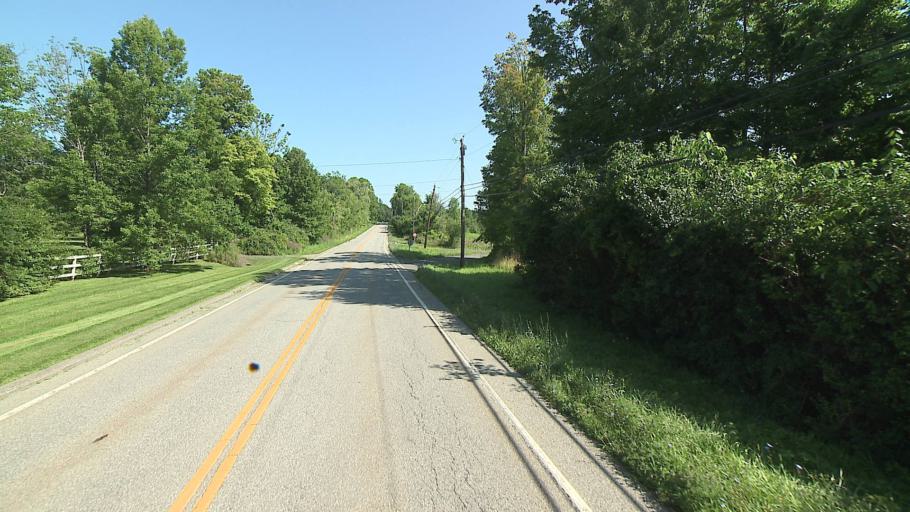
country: US
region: Connecticut
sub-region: Litchfield County
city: Kent
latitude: 41.8503
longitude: -73.4923
